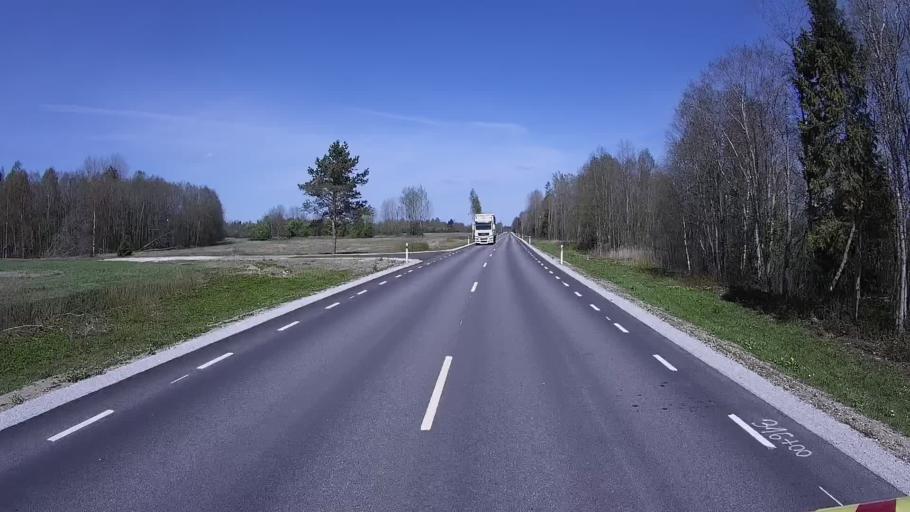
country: EE
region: Harju
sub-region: Nissi vald
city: Turba
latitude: 59.1577
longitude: 24.0738
